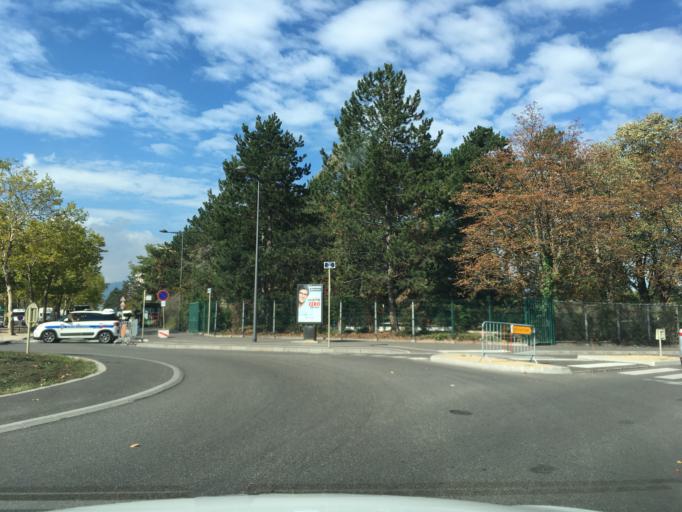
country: FR
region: Alsace
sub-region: Departement du Haut-Rhin
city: Colmar
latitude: 48.0784
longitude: 7.3331
